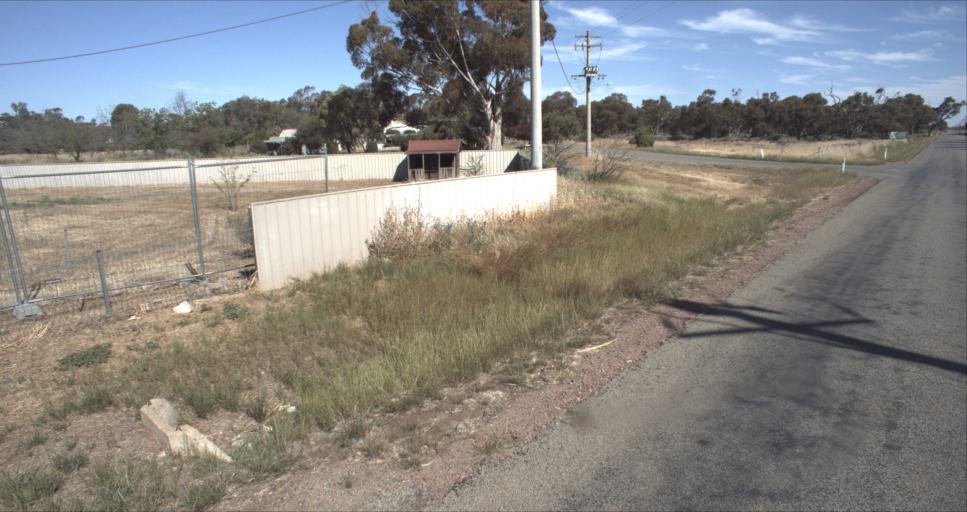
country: AU
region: New South Wales
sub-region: Leeton
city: Leeton
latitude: -34.5558
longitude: 146.3845
